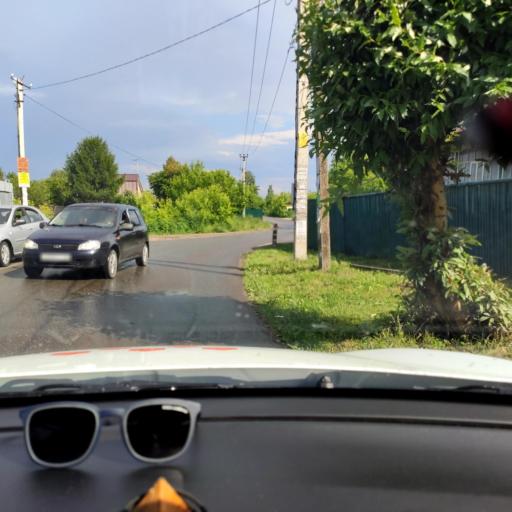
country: RU
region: Tatarstan
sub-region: Zelenodol'skiy Rayon
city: Vasil'yevo
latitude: 55.8330
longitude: 48.7246
